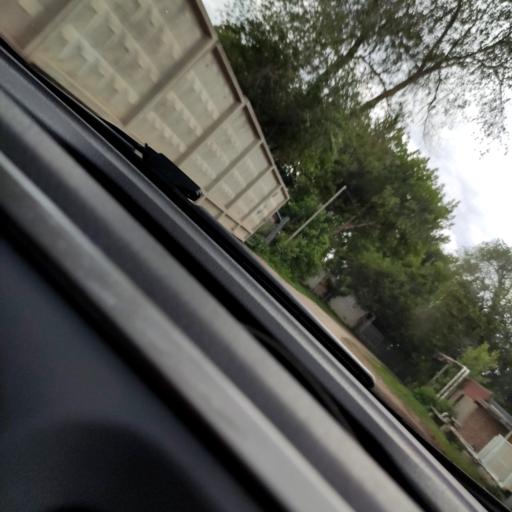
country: RU
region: Samara
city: Tol'yatti
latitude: 53.5327
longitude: 49.2561
